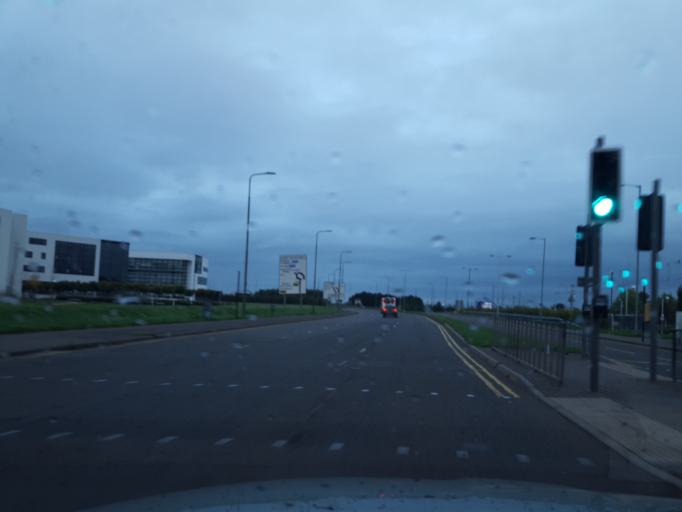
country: GB
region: Scotland
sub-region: Edinburgh
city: Currie
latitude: 55.9372
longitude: -3.3173
